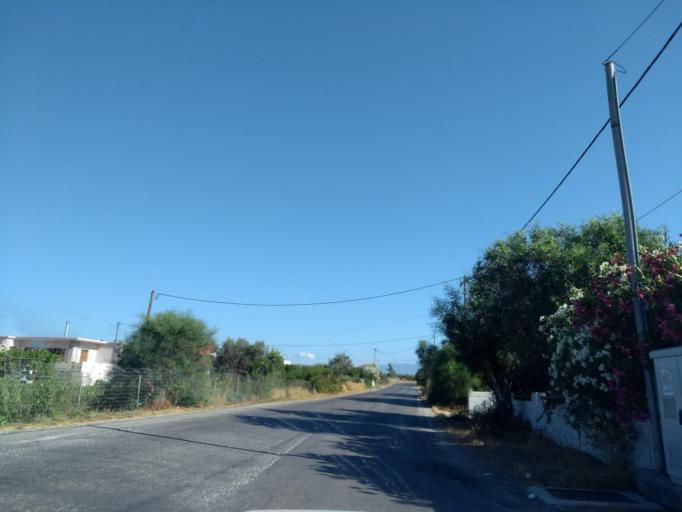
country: GR
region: Crete
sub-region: Nomos Chanias
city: Pithari
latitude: 35.5798
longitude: 24.0936
